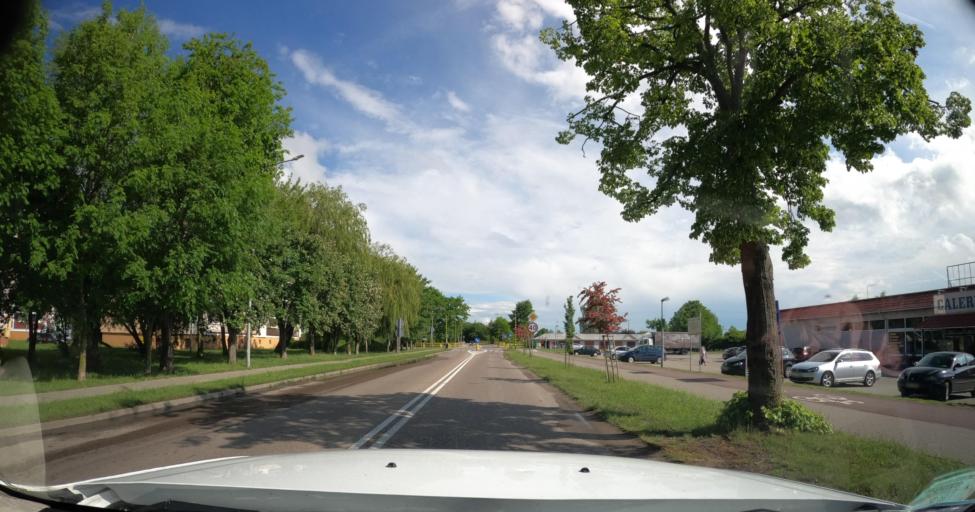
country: PL
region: Pomeranian Voivodeship
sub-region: Powiat nowodworski
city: Nowy Dwor Gdanski
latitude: 54.2097
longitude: 19.1118
